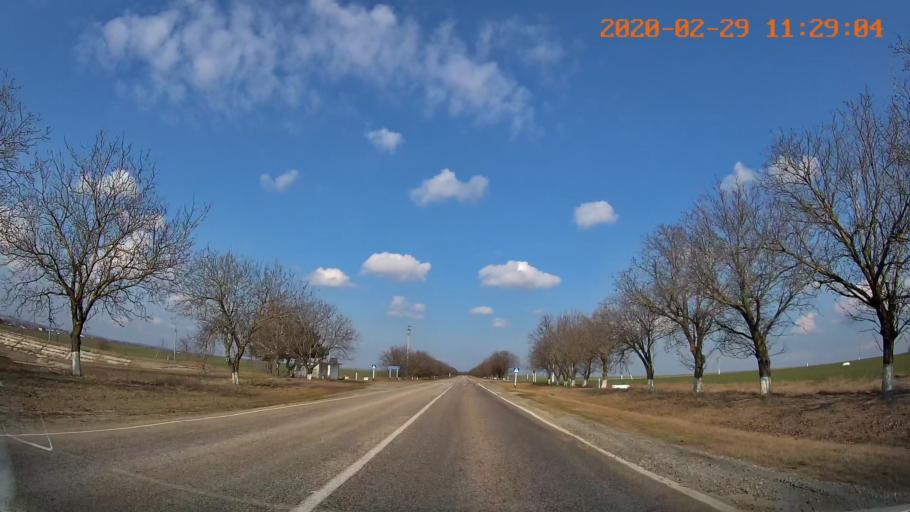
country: MD
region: Telenesti
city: Cocieri
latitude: 47.4888
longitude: 29.1287
